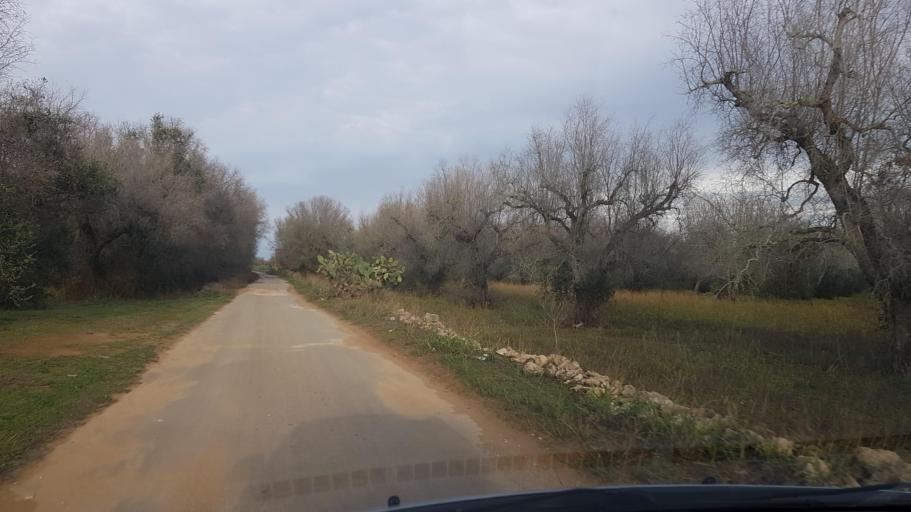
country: IT
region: Apulia
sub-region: Provincia di Brindisi
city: Torchiarolo
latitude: 40.4933
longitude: 18.0716
